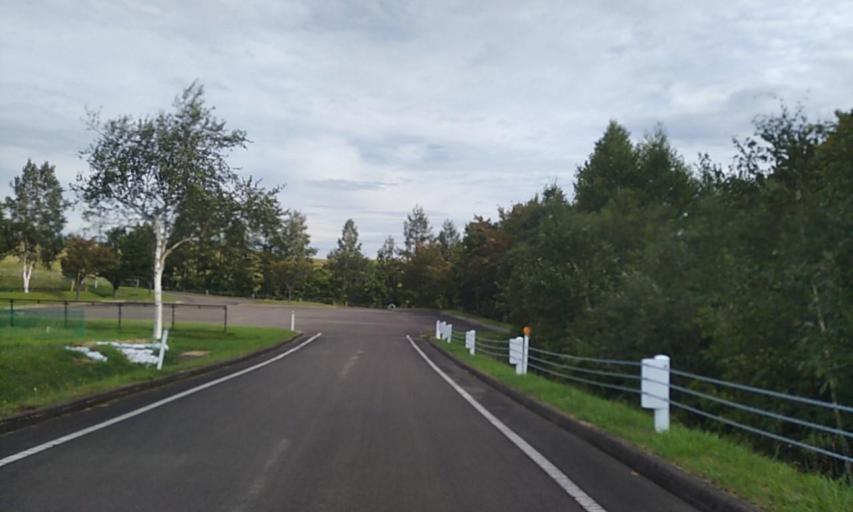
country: JP
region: Hokkaido
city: Abashiri
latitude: 43.7957
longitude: 144.5744
